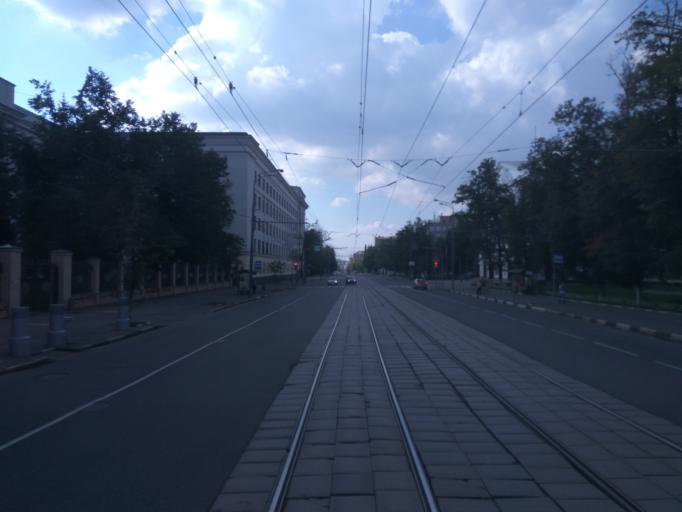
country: RU
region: Moscow
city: Lefortovo
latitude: 55.7540
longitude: 37.7093
